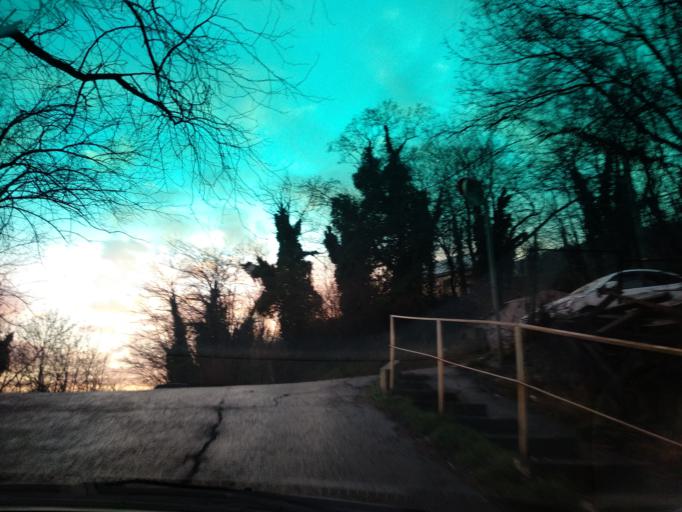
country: RU
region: Krasnodarskiy
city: Tuapse
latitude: 44.1073
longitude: 39.0805
